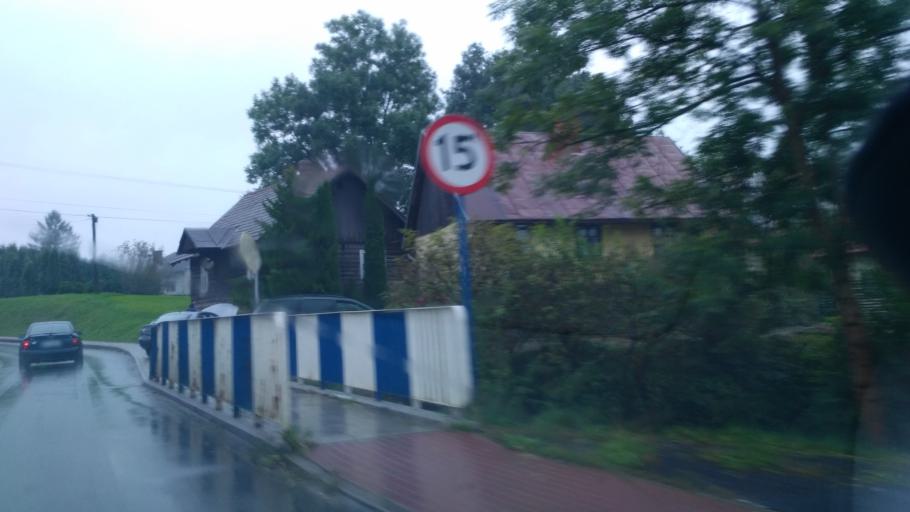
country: PL
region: Subcarpathian Voivodeship
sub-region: Powiat krosnienski
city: Korczyna
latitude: 49.7134
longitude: 21.8123
